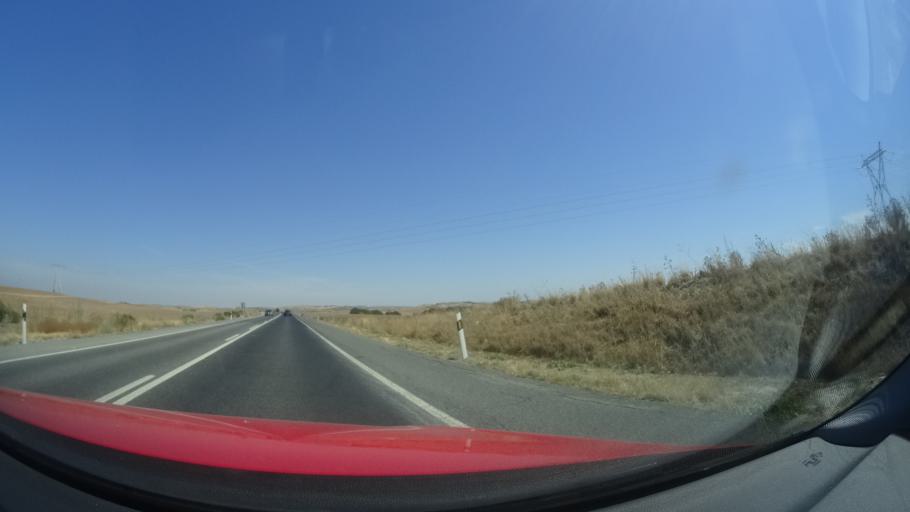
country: ES
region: Andalusia
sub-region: Provincia de Sevilla
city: Las Cabezas de San Juan
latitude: 36.9424
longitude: -5.9110
